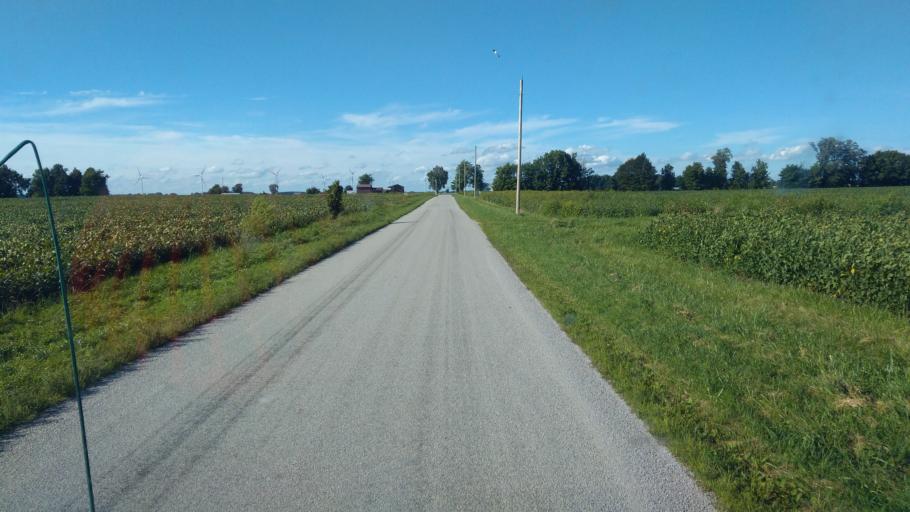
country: US
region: Ohio
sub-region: Hardin County
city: Ada
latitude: 40.7663
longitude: -83.7095
